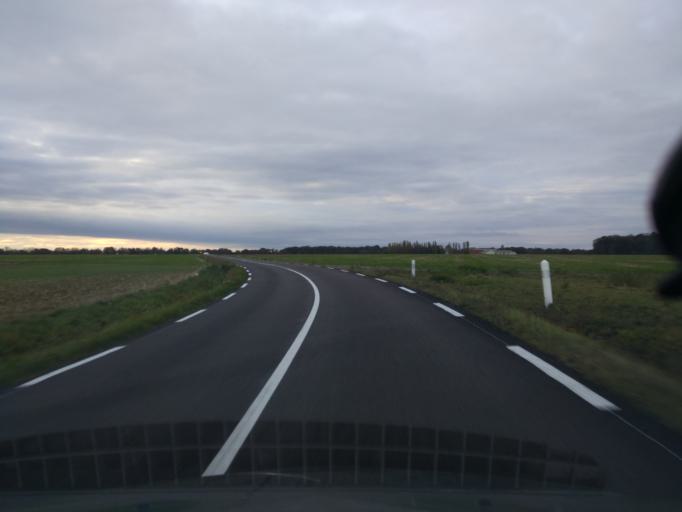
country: FR
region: Ile-de-France
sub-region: Departement de l'Essonne
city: Les Molieres
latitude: 48.6624
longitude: 2.0648
